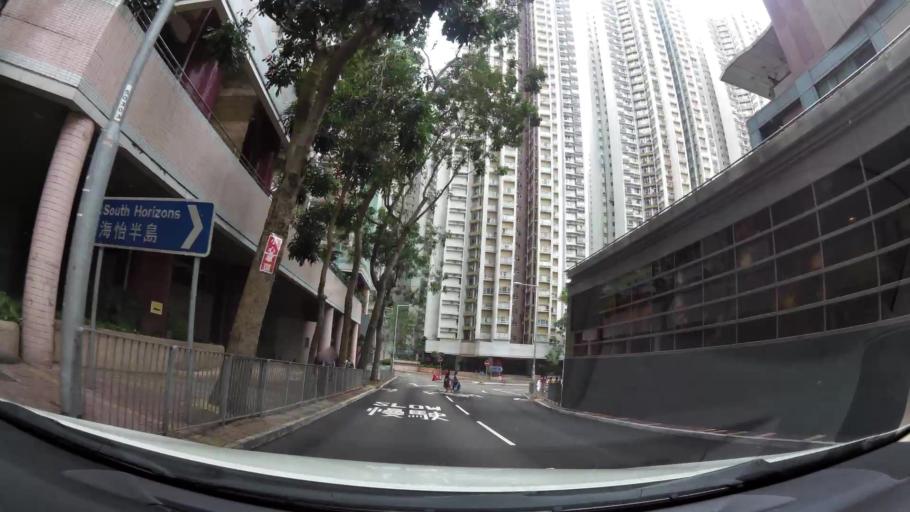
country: HK
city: Yung Shue Wan
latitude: 22.2435
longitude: 114.1489
